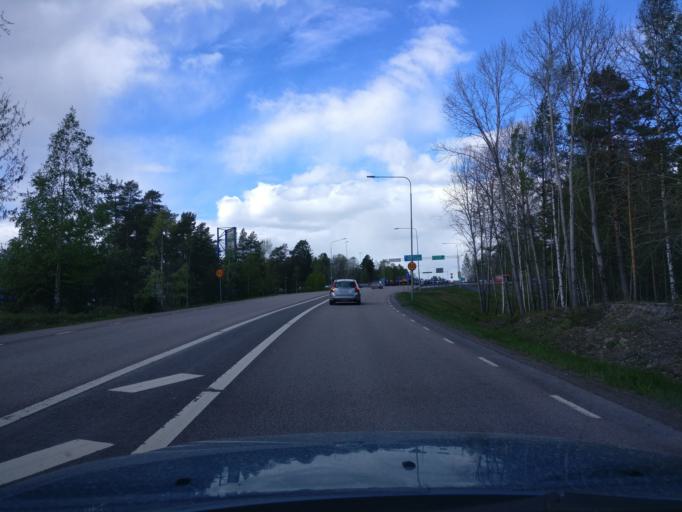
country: SE
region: Vaermland
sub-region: Hammaro Kommun
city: Skoghall
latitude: 59.3757
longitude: 13.4408
